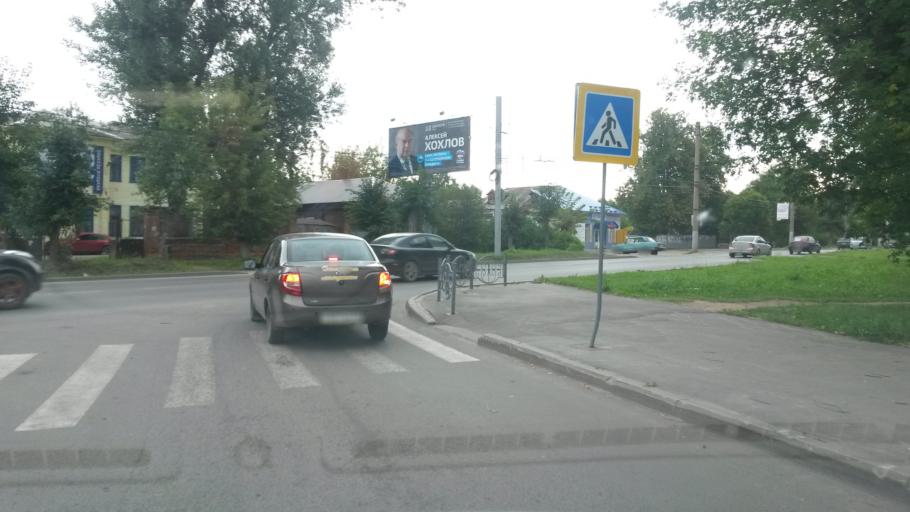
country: RU
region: Ivanovo
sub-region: Gorod Ivanovo
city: Ivanovo
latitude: 57.0205
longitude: 40.9521
